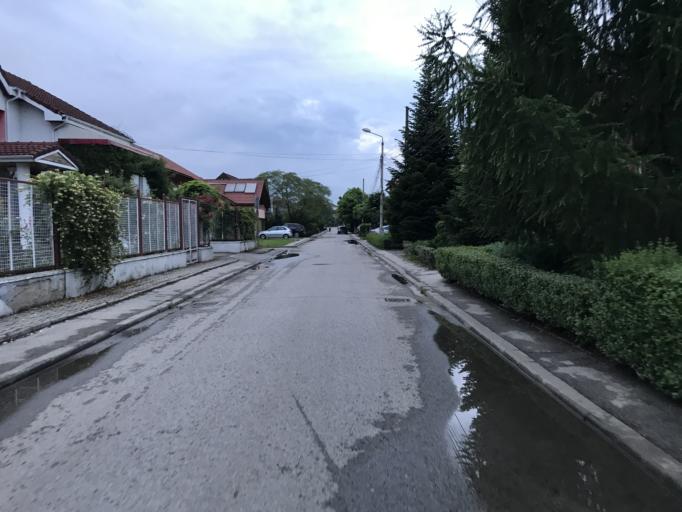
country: RO
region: Timis
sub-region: Comuna Dumbravita
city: Dumbravita
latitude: 45.7814
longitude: 21.2360
